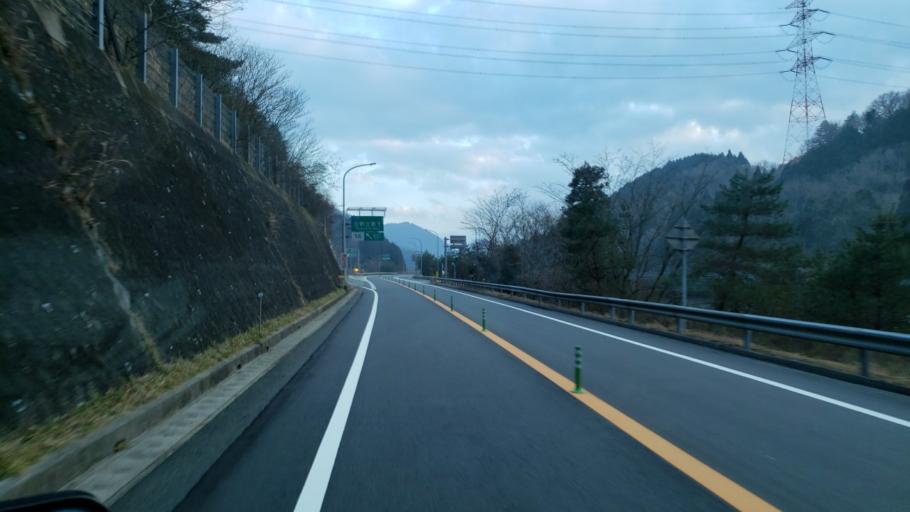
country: JP
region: Hyogo
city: Nishiwaki
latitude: 35.1837
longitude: 134.7923
